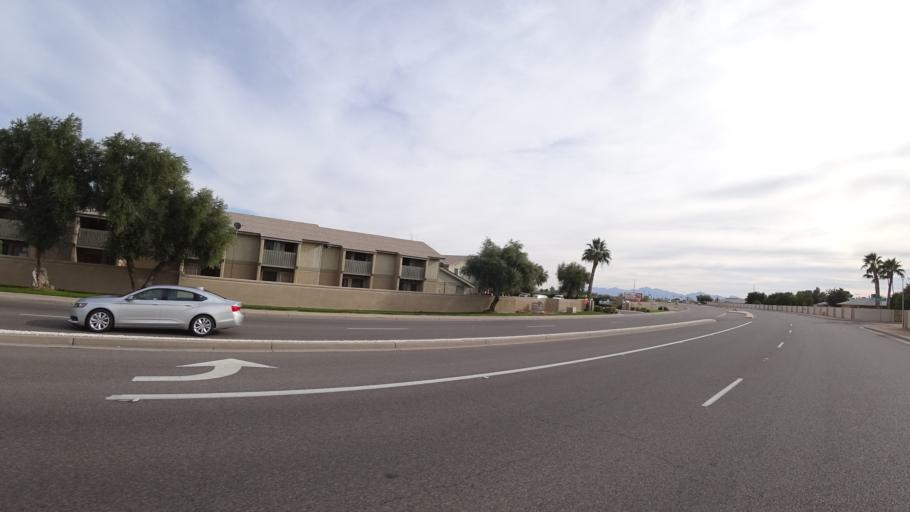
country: US
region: Arizona
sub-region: Maricopa County
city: Sun City
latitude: 33.5691
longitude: -112.2757
